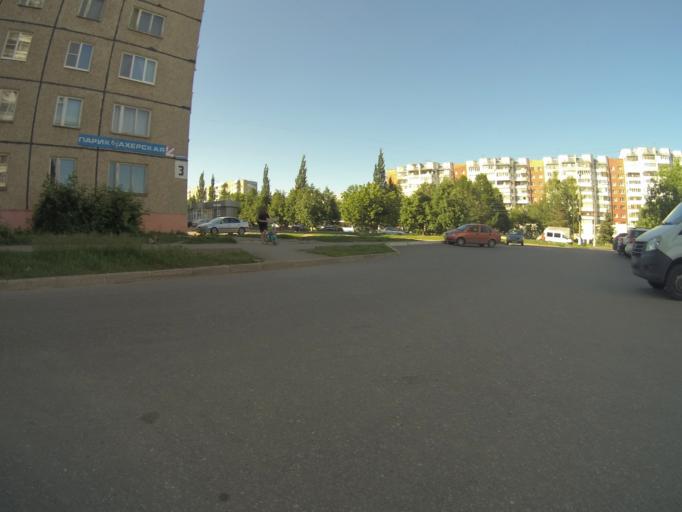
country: RU
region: Vladimir
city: Kommunar
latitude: 56.1618
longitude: 40.4711
